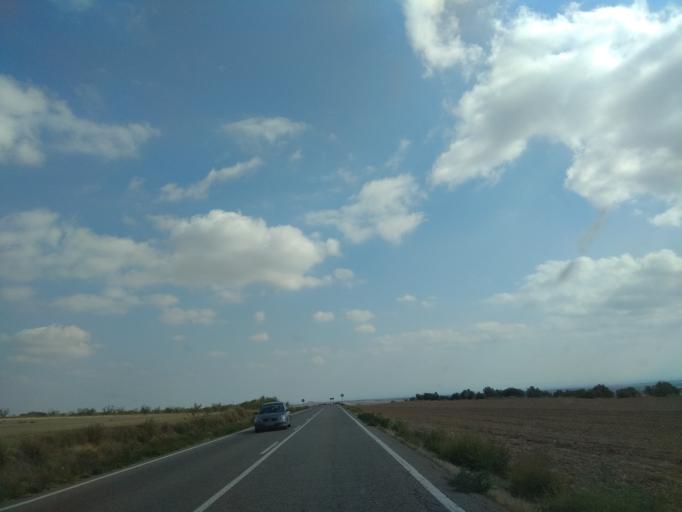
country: ES
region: Catalonia
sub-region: Provincia de Lleida
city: Algerri
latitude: 41.8092
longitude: 0.6565
